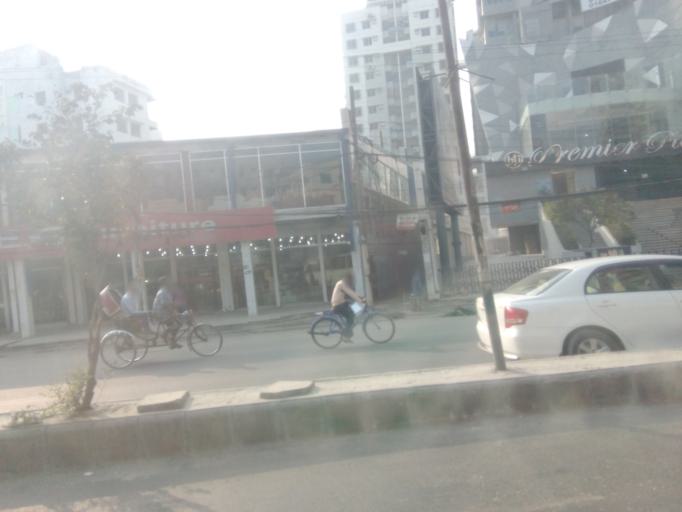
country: BD
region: Dhaka
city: Paltan
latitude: 23.7886
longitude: 90.4249
